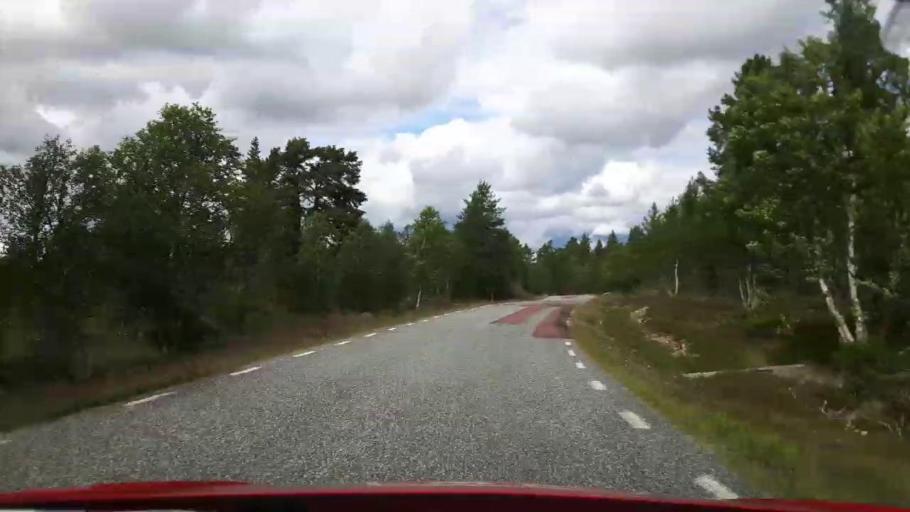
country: NO
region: Hedmark
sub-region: Trysil
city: Innbygda
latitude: 62.1107
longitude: 12.9777
